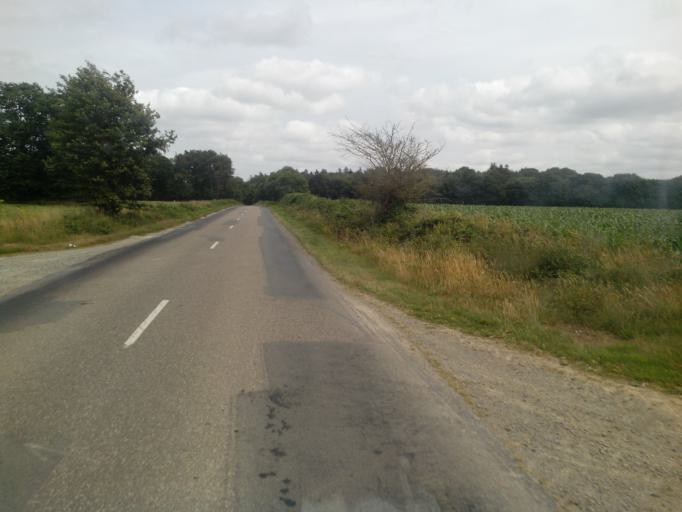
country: FR
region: Brittany
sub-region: Departement d'Ille-et-Vilaine
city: Maxent
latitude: 47.9890
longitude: -2.0594
